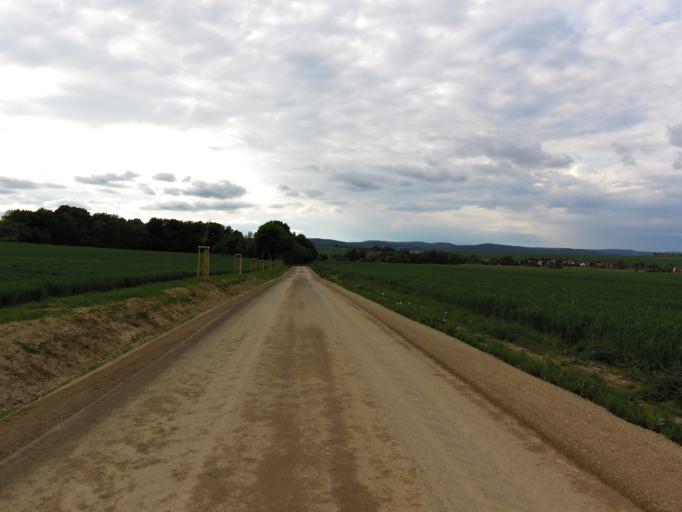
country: DE
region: Thuringia
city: Dippach
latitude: 50.9158
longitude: 10.0885
